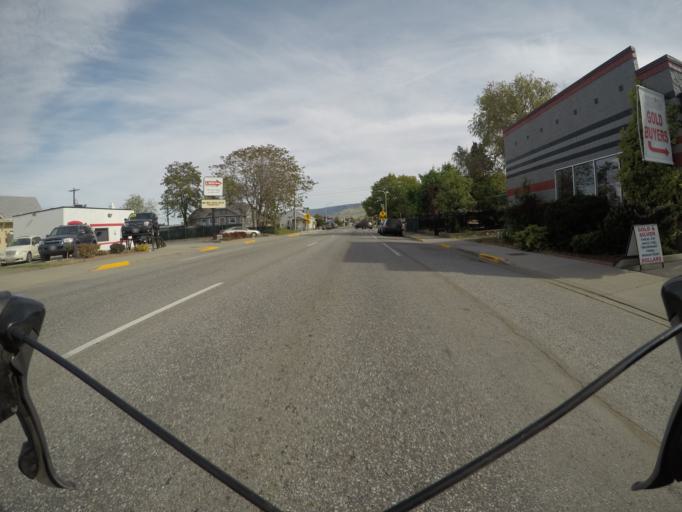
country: US
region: Washington
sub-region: Chelan County
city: Wenatchee
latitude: 47.4180
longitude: -120.3094
